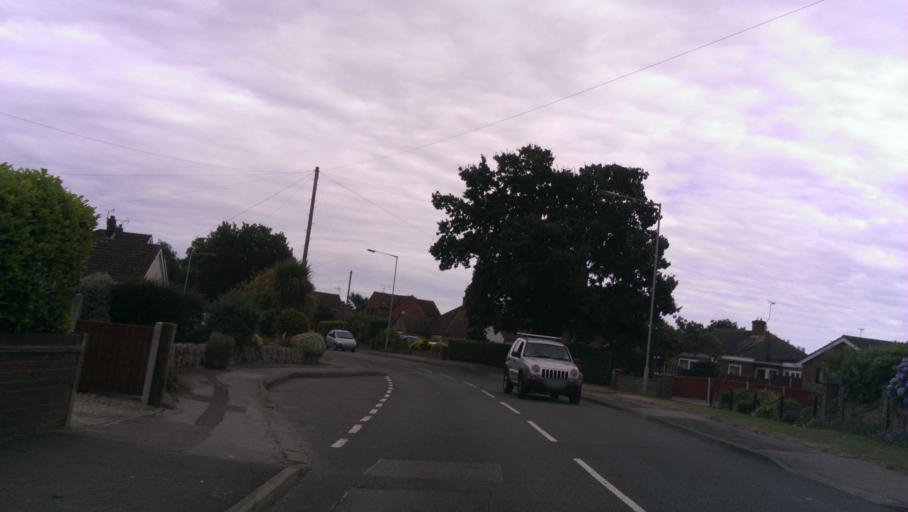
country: GB
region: England
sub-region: Essex
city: Eight Ash Green
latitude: 51.8781
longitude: 0.8394
